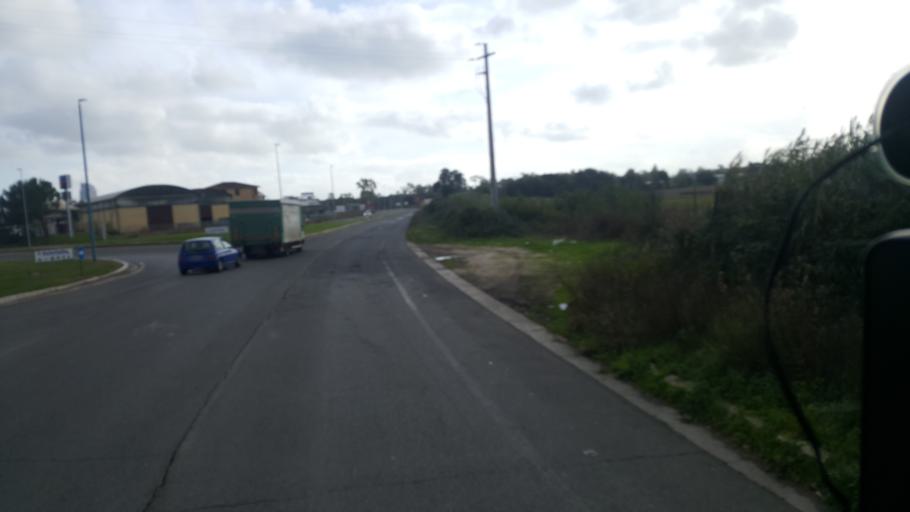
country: IT
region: Latium
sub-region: Provincia di Latina
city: Latina
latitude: 41.4777
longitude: 12.8740
